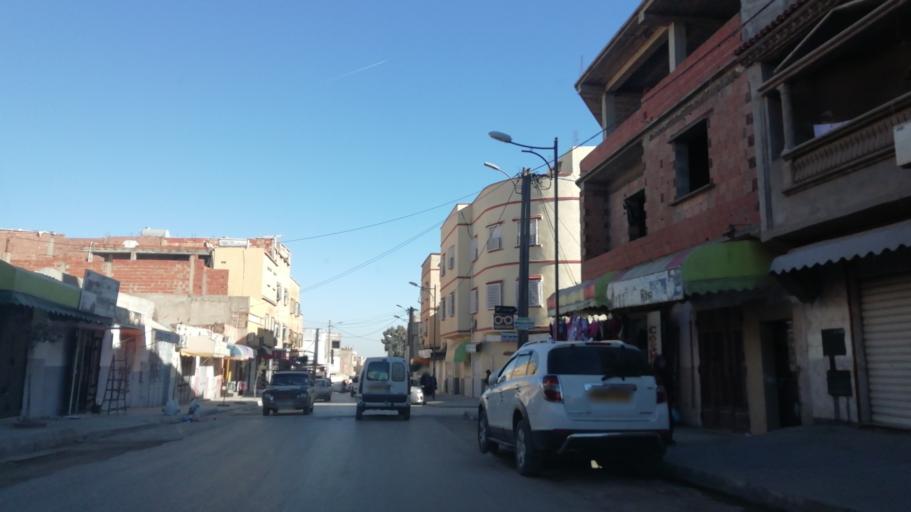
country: DZ
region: Oran
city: Bir el Djir
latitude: 35.7254
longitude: -0.5381
